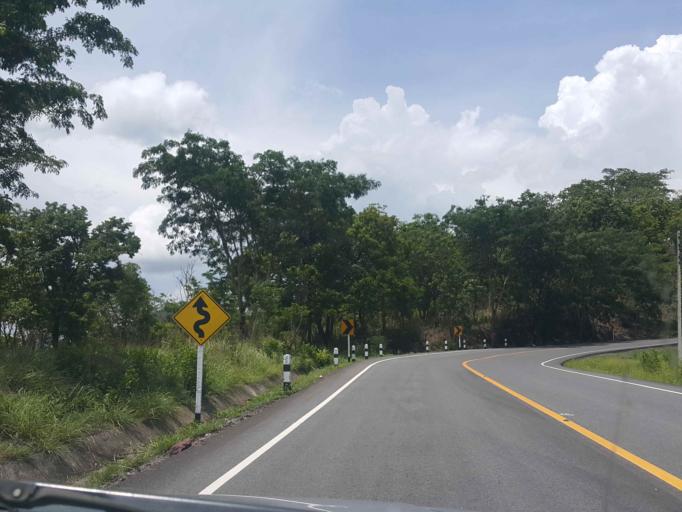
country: TH
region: Phayao
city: Chiang Muan
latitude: 18.8471
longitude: 100.3361
